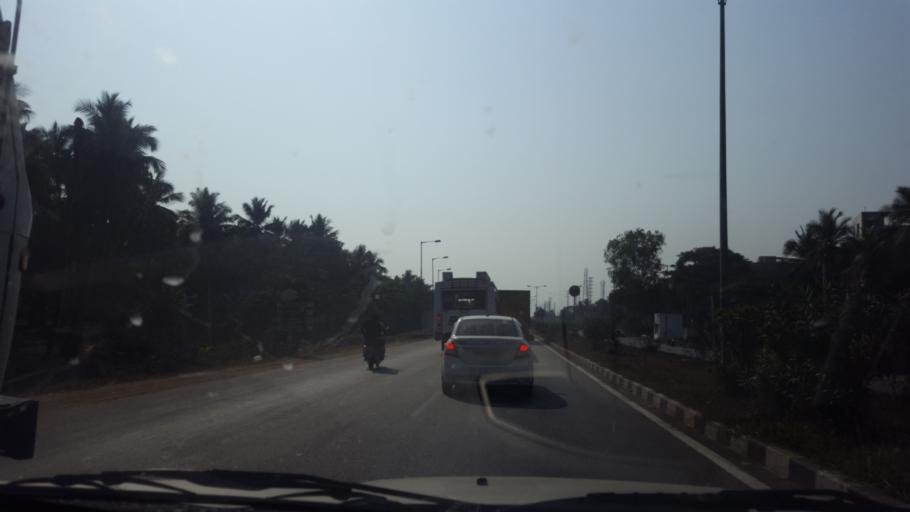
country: IN
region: Andhra Pradesh
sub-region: Vishakhapatnam
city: Anakapalle
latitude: 17.6749
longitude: 83.0069
